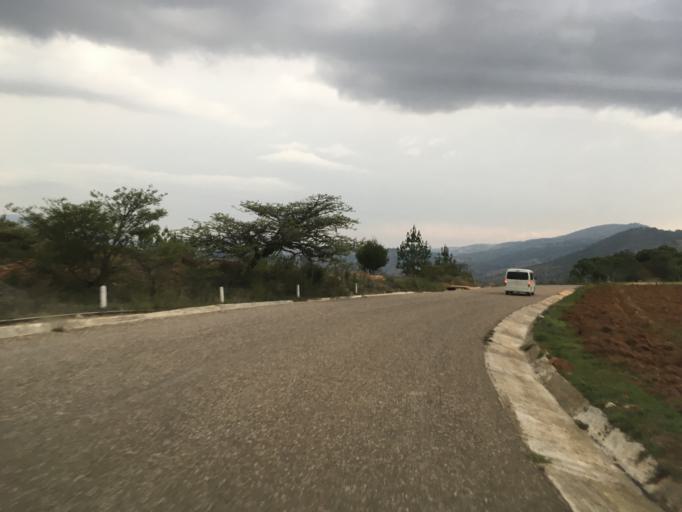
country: MX
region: Oaxaca
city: Santiago Tilantongo
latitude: 17.2428
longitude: -97.3073
